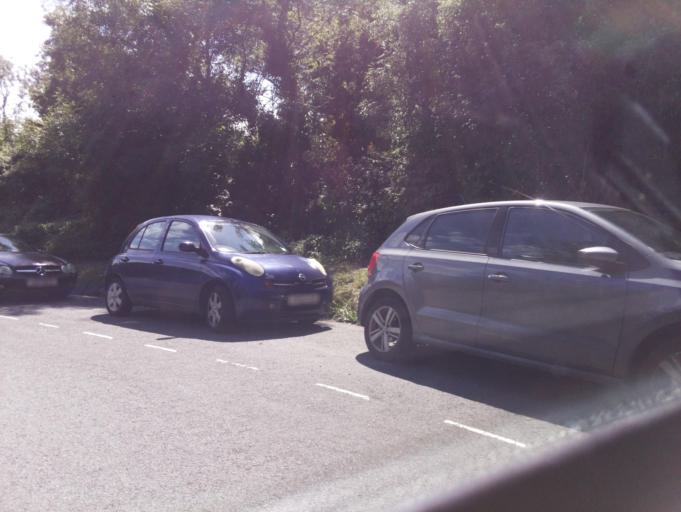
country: GB
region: England
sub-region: Bristol
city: Bristol
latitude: 51.4634
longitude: -2.6274
